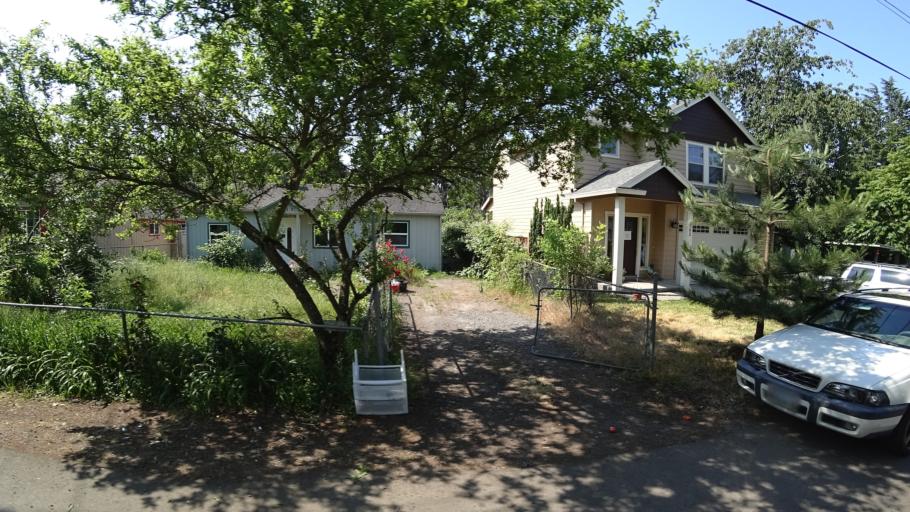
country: US
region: Oregon
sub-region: Multnomah County
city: Lents
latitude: 45.4549
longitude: -122.5945
